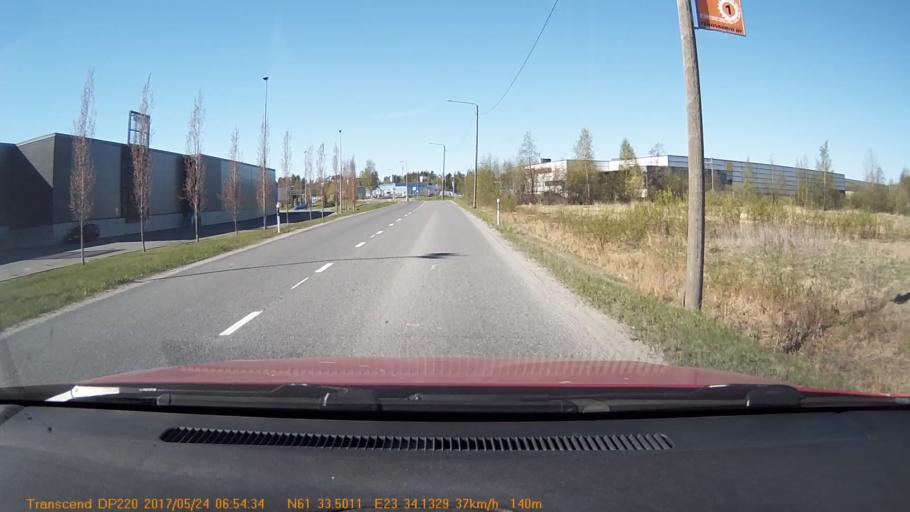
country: FI
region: Pirkanmaa
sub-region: Tampere
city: Yloejaervi
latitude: 61.5584
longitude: 23.5690
